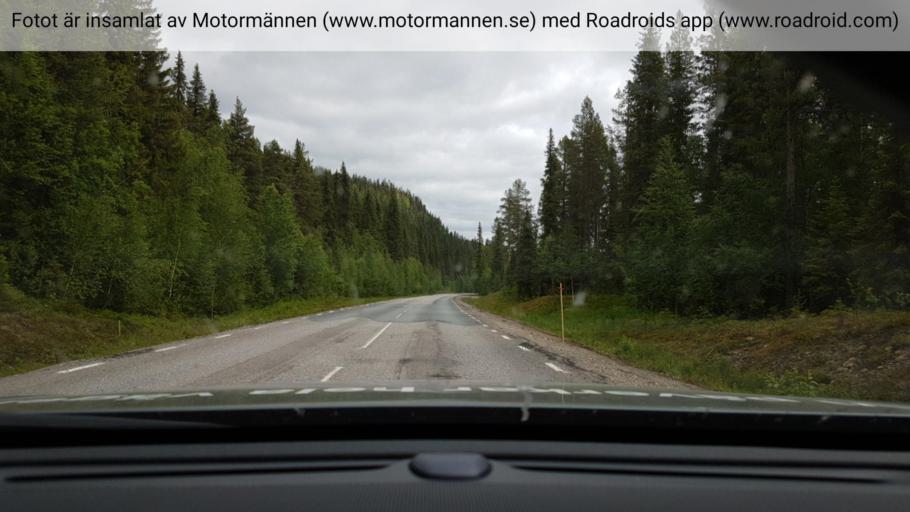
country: SE
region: Vaesterbotten
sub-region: Storumans Kommun
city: Fristad
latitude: 65.8196
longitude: 16.8415
